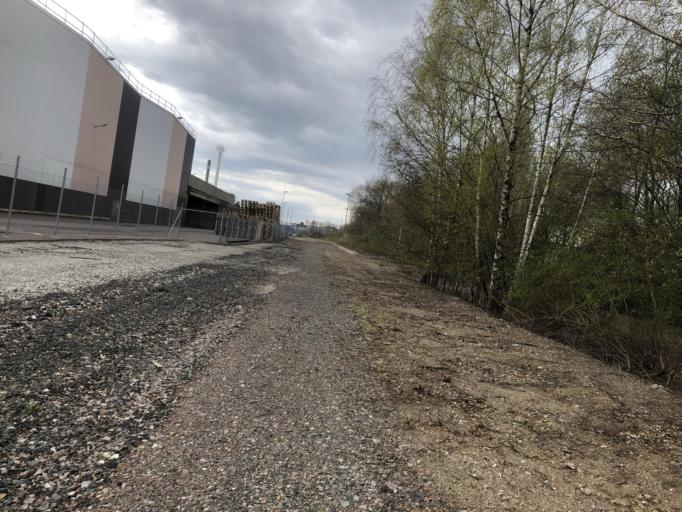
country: SE
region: Skane
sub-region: Malmo
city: Oxie
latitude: 55.5534
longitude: 13.0528
